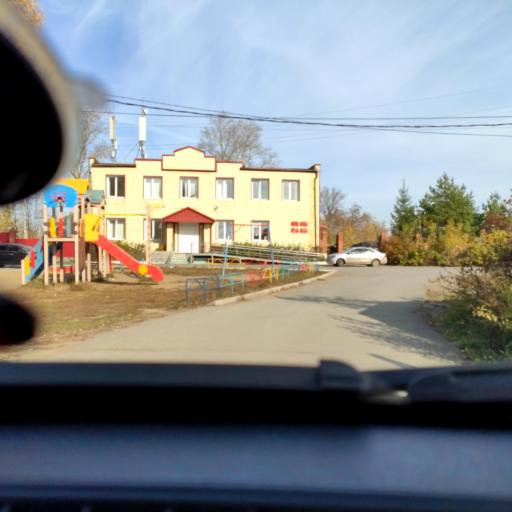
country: RU
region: Bashkortostan
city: Ufa
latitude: 54.7360
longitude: 55.9132
